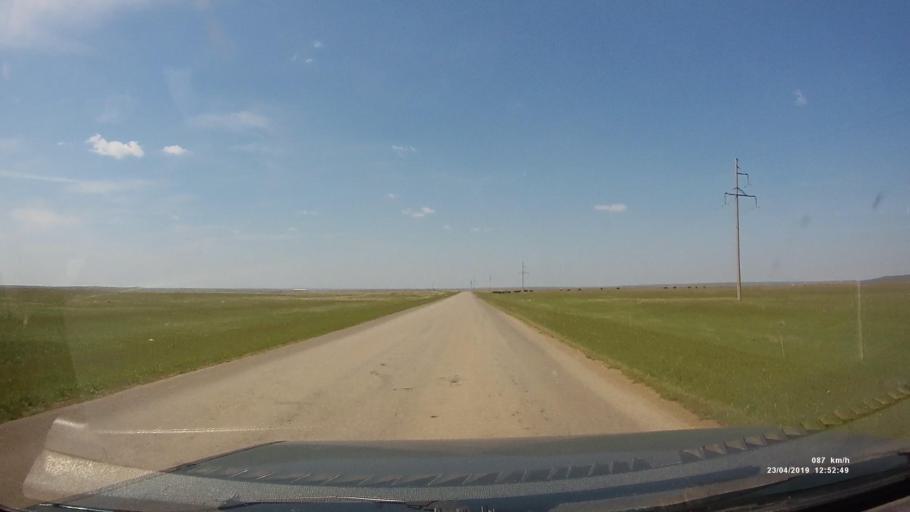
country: RU
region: Kalmykiya
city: Yashalta
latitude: 46.5683
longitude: 42.6046
